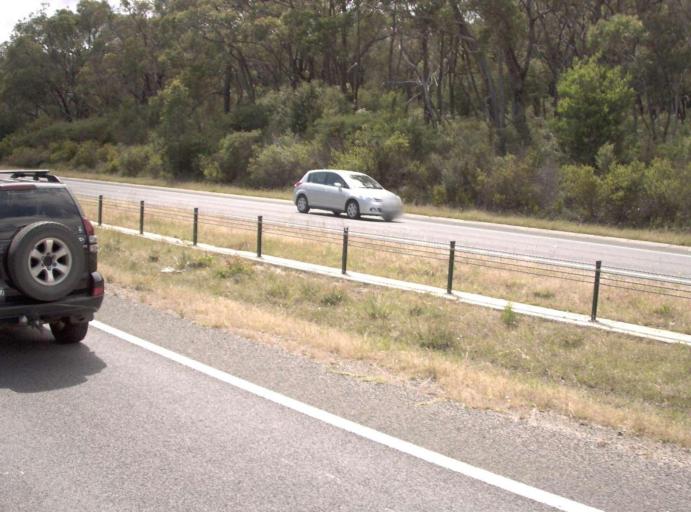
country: AU
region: Victoria
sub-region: Cardinia
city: Koo-Wee-Rup
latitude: -38.3874
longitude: 145.5465
